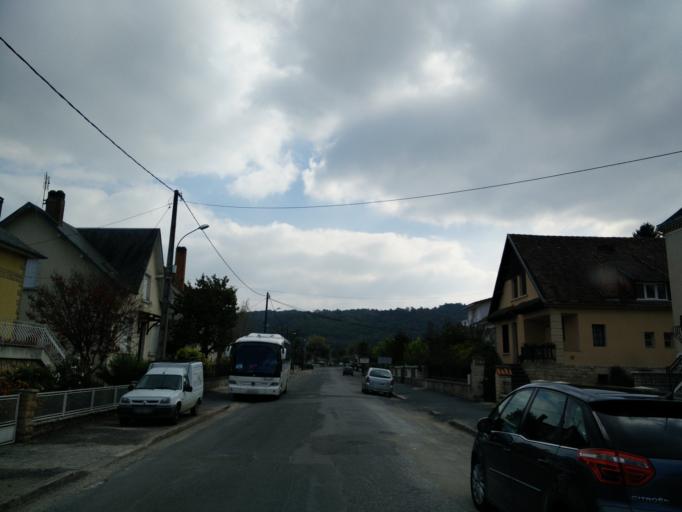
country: FR
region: Aquitaine
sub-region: Departement de la Dordogne
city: Montignac
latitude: 45.0647
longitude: 1.1656
